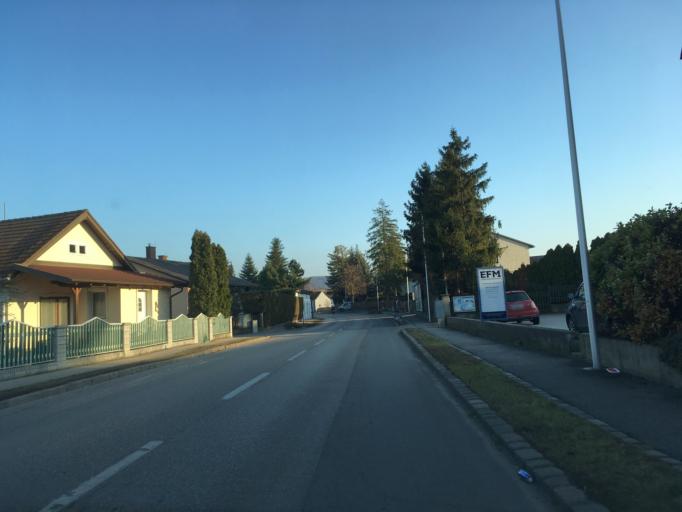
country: AT
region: Lower Austria
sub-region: Politischer Bezirk Tulln
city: Konigstetten
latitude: 48.3321
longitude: 16.1560
